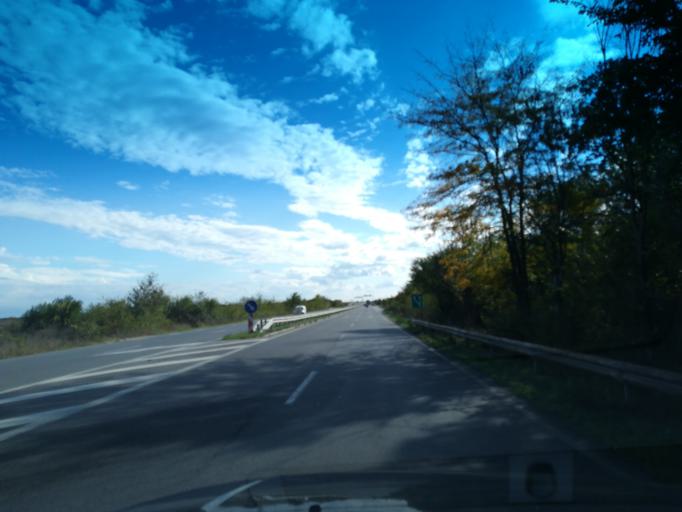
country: BG
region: Stara Zagora
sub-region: Obshtina Stara Zagora
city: Stara Zagora
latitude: 42.3454
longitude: 25.6602
